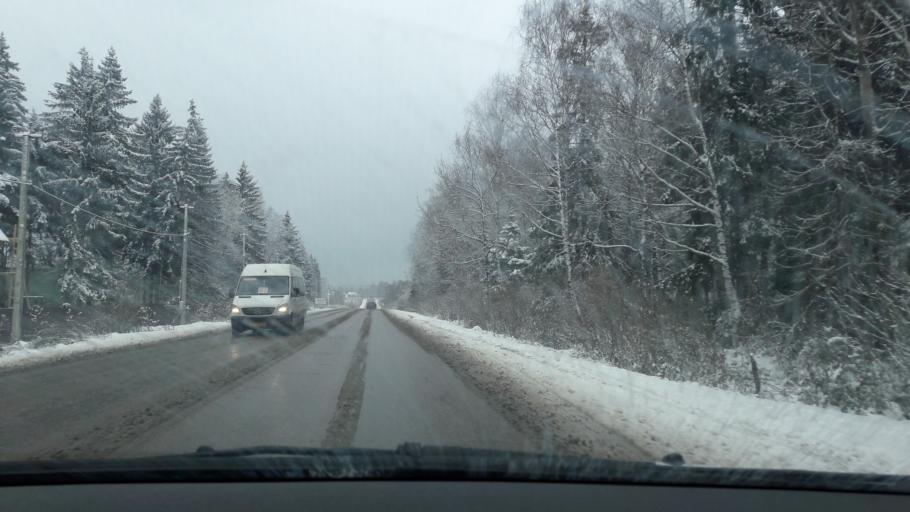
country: RU
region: Moskovskaya
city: Zvenigorod
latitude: 55.6286
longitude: 36.8636
